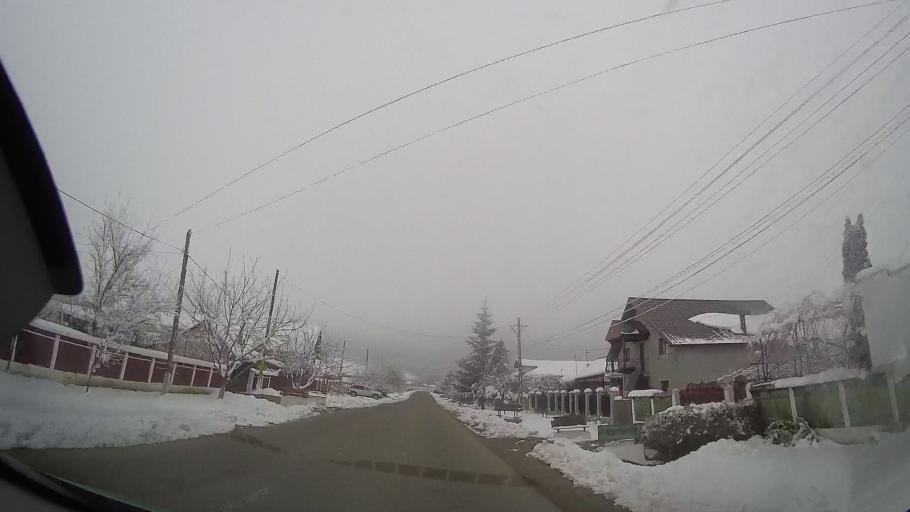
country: RO
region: Neamt
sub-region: Comuna Valea Ursului
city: Valea Ursului
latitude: 46.8504
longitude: 27.0486
